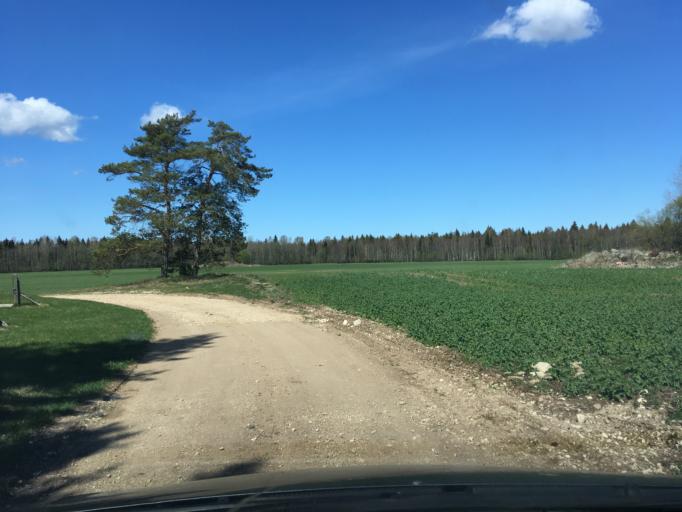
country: EE
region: Harju
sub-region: Raasiku vald
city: Raasiku
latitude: 59.2229
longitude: 25.1508
